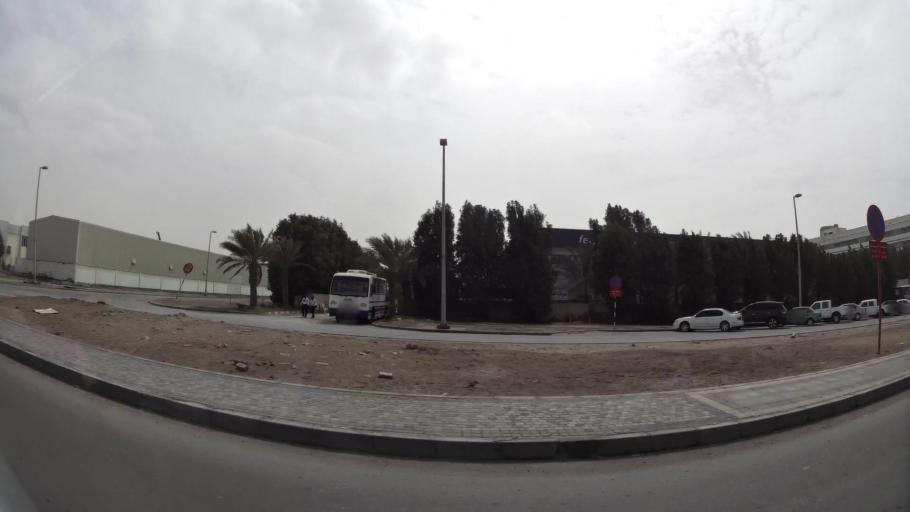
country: AE
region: Abu Dhabi
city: Abu Dhabi
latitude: 24.3583
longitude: 54.4775
